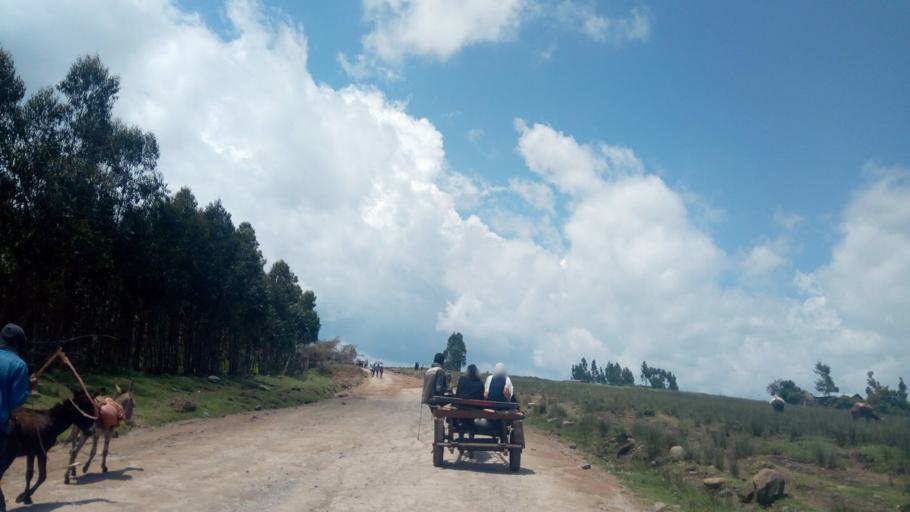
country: ET
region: Oromiya
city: Sendafa
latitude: 8.9808
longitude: 39.1248
